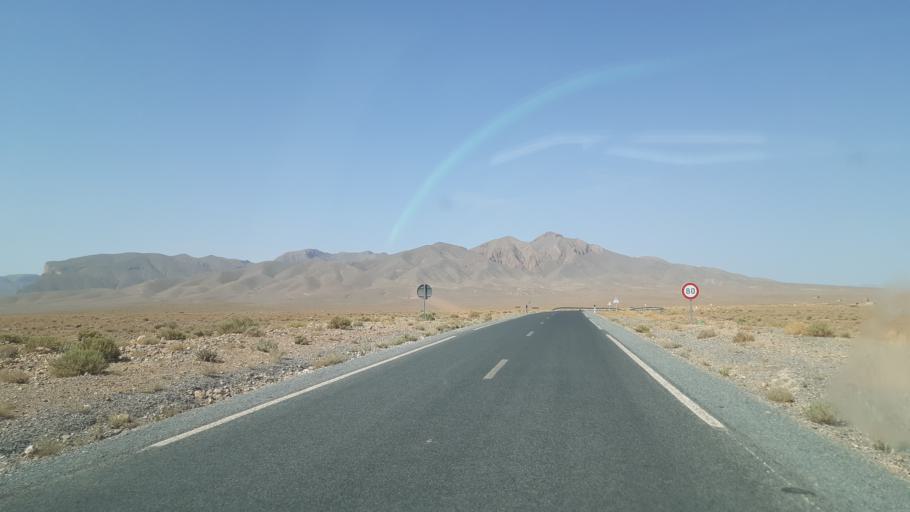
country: MA
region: Meknes-Tafilalet
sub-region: Errachidia
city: Amouguer
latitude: 32.2234
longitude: -4.6724
